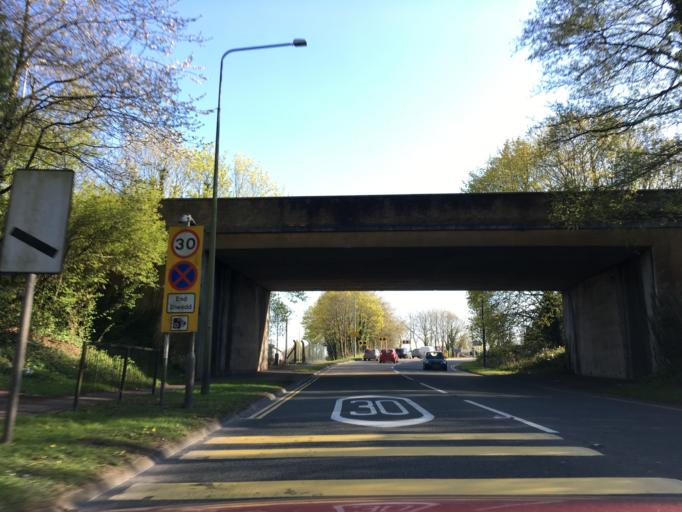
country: GB
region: Wales
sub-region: Torfaen County Borough
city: Cwmbran
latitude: 51.6450
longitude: -3.0226
